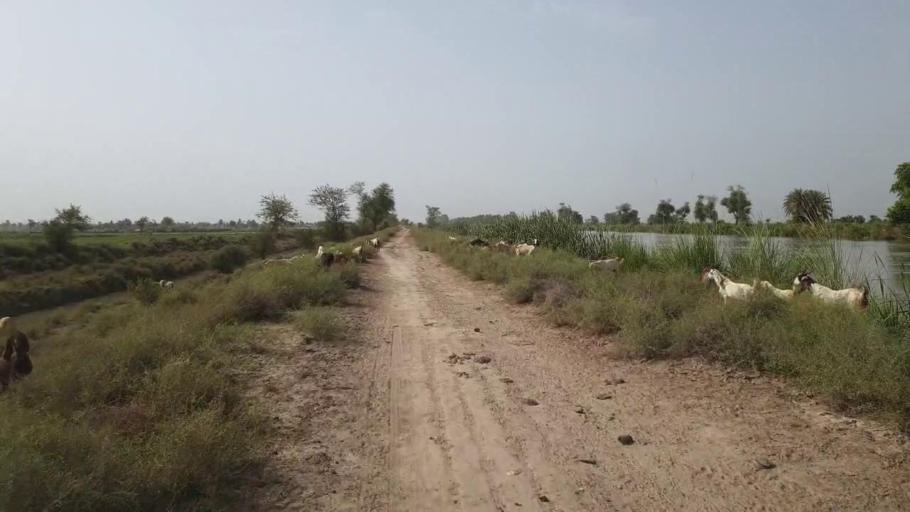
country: PK
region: Sindh
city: Daur
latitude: 26.4397
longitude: 68.1617
